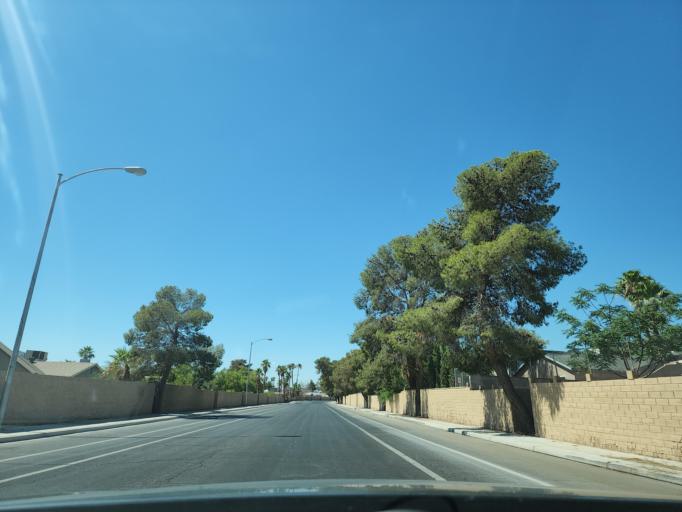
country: US
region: Nevada
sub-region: Clark County
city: Spring Valley
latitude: 36.1126
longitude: -115.2520
